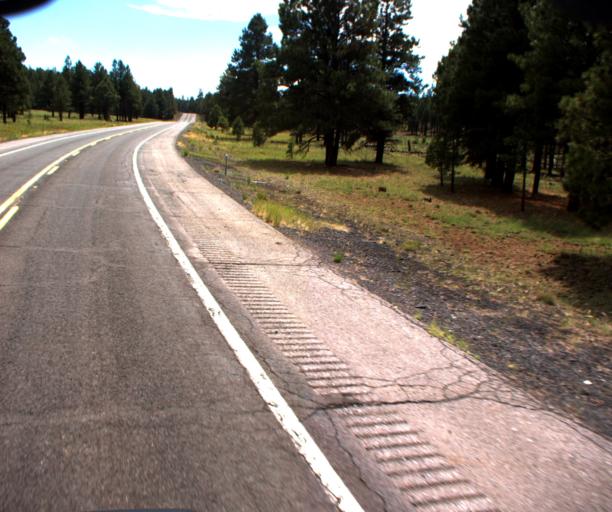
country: US
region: Arizona
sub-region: Coconino County
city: Parks
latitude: 35.4422
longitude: -111.7614
